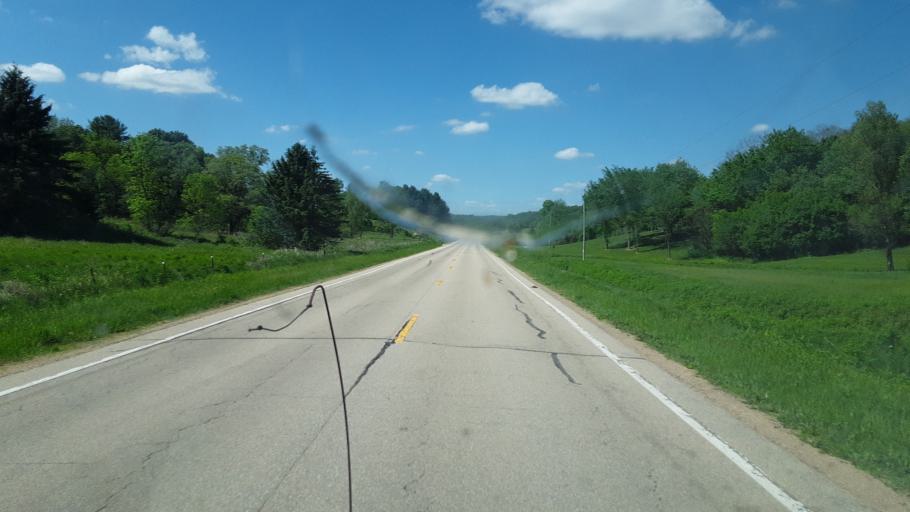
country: US
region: Wisconsin
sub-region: Sauk County
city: Reedsburg
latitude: 43.4941
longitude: -90.2036
